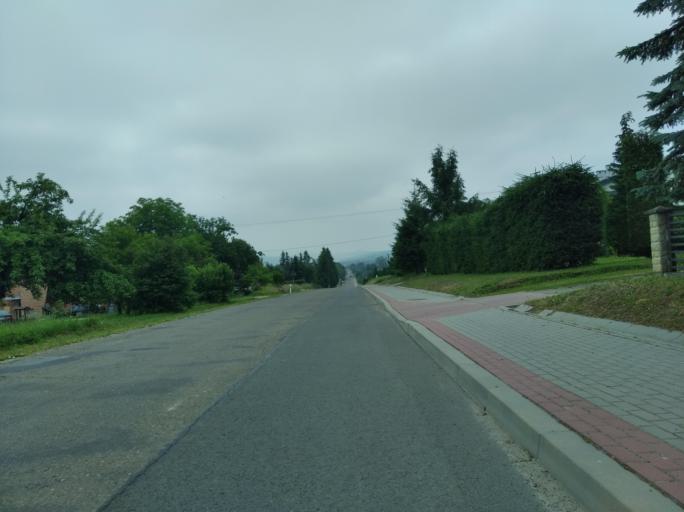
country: PL
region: Subcarpathian Voivodeship
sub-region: Powiat krosnienski
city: Sieniawa
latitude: 49.5782
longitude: 21.9236
